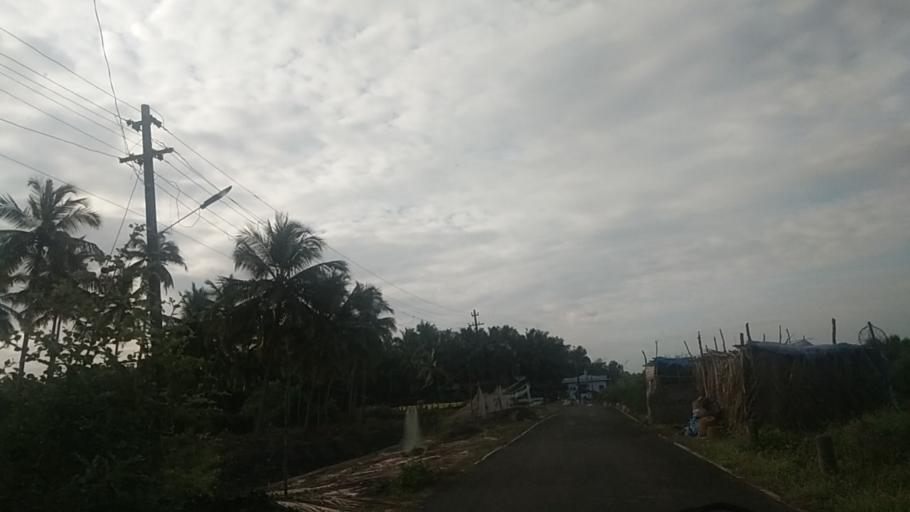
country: IN
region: Goa
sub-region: South Goa
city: Cavelossim
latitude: 15.1772
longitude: 73.9624
